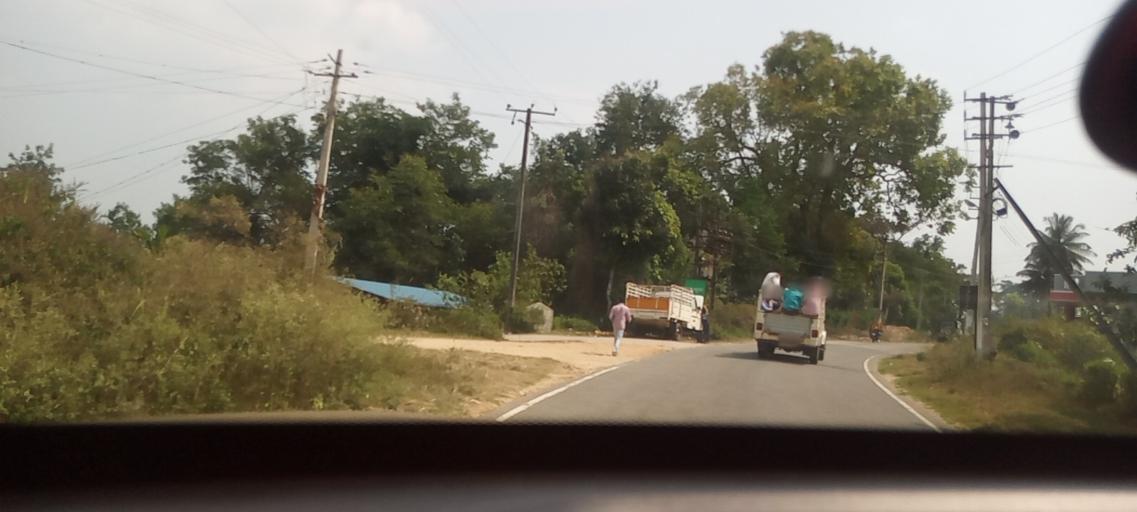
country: IN
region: Karnataka
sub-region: Chikmagalur
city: Mudigere
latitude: 13.2508
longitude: 75.6413
